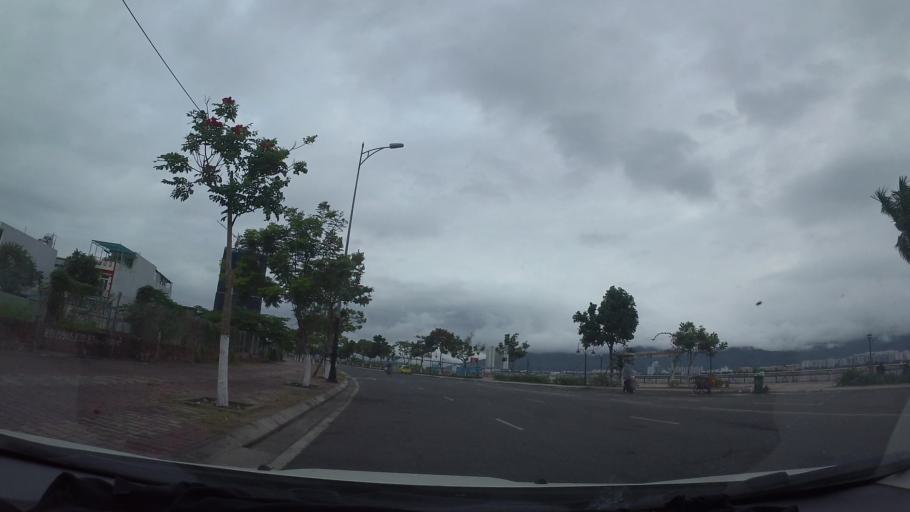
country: VN
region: Da Nang
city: Da Nang
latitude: 16.0830
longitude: 108.2233
